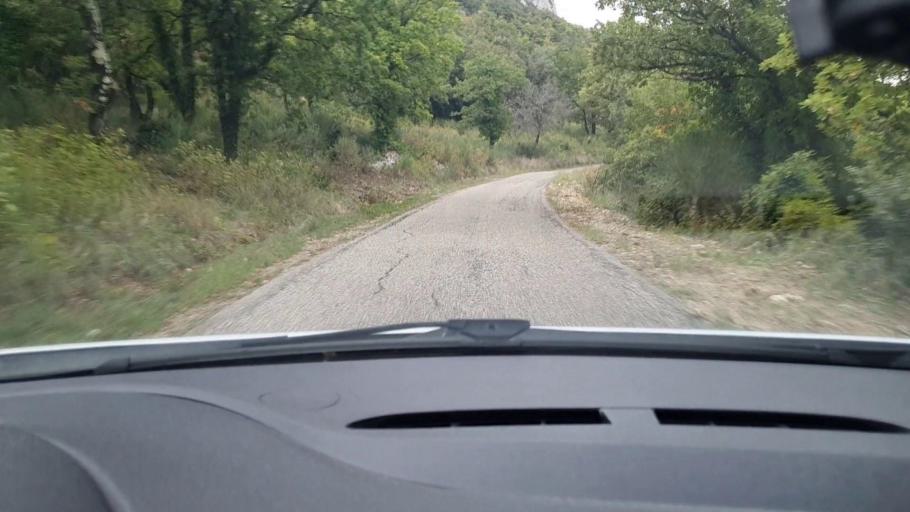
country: FR
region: Languedoc-Roussillon
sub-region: Departement du Gard
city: Mons
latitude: 44.1370
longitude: 4.2888
